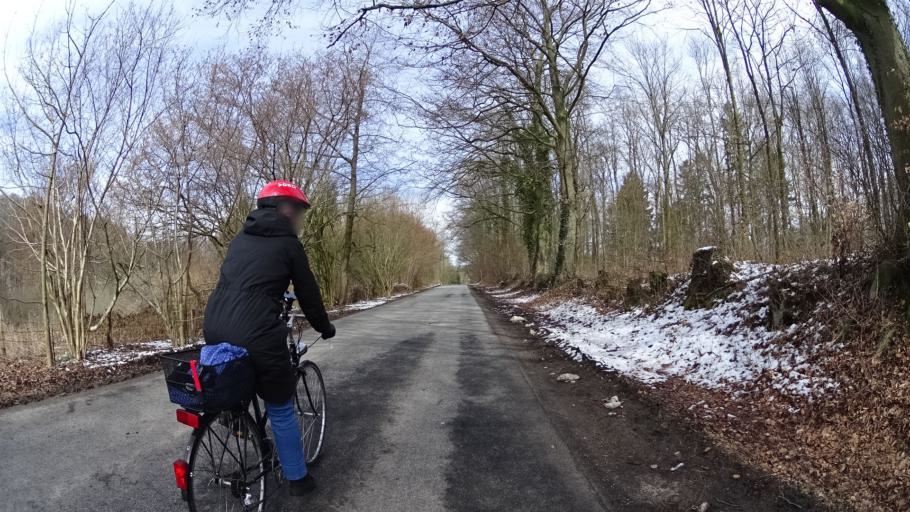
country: DE
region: Schleswig-Holstein
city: Stolpe
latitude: 54.1406
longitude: 10.2300
